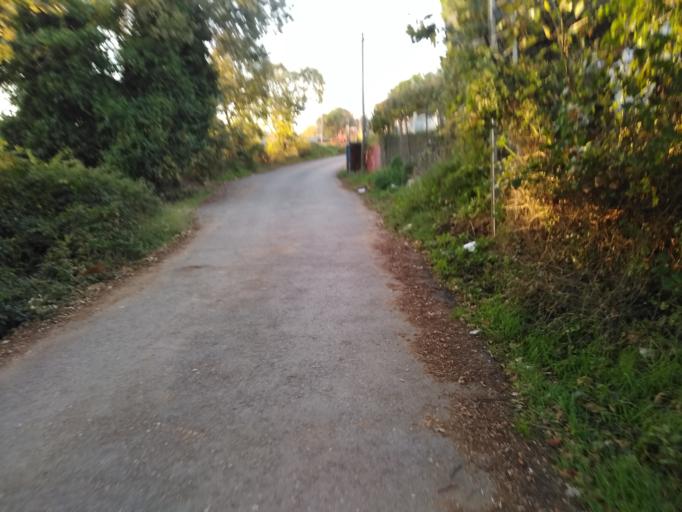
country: TR
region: Istanbul
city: Arikoey
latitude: 41.2391
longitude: 28.9844
